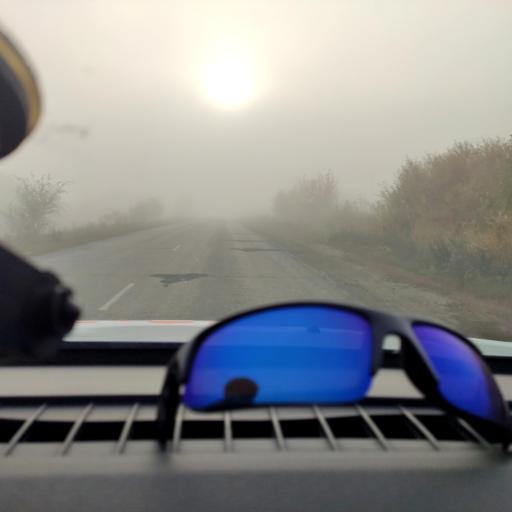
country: RU
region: Samara
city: Chapayevsk
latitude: 53.0047
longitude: 49.7462
